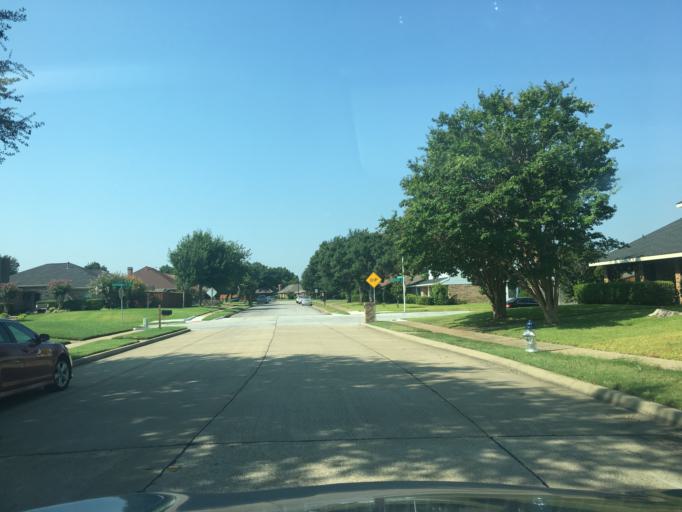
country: US
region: Texas
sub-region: Dallas County
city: Garland
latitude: 32.9491
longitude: -96.6311
